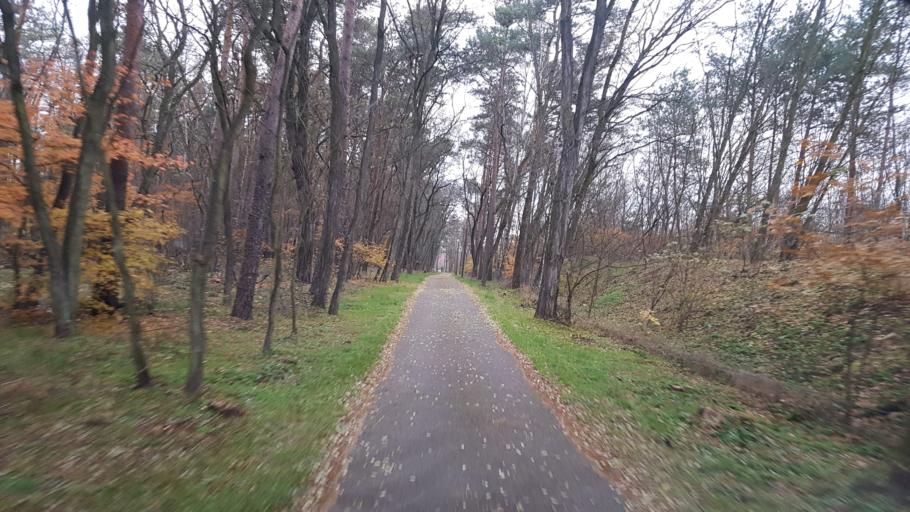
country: DE
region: Brandenburg
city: Calau
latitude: 51.7320
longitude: 13.9793
